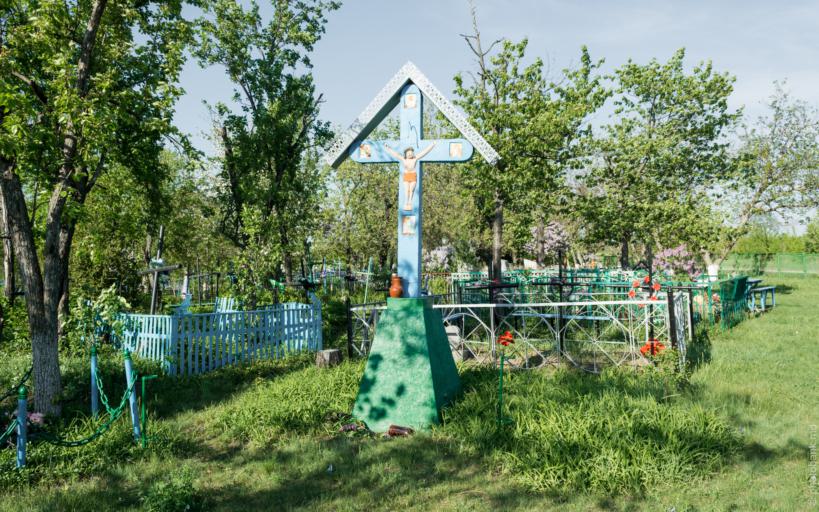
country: MD
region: Balti
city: Balti
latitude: 47.7112
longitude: 27.8755
